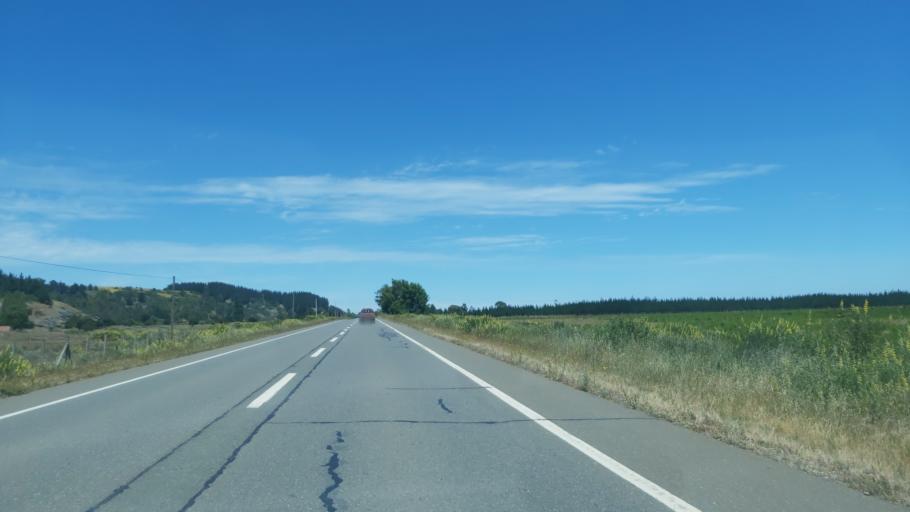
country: CL
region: Maule
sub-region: Provincia de Talca
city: Constitucion
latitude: -35.1625
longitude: -72.2571
